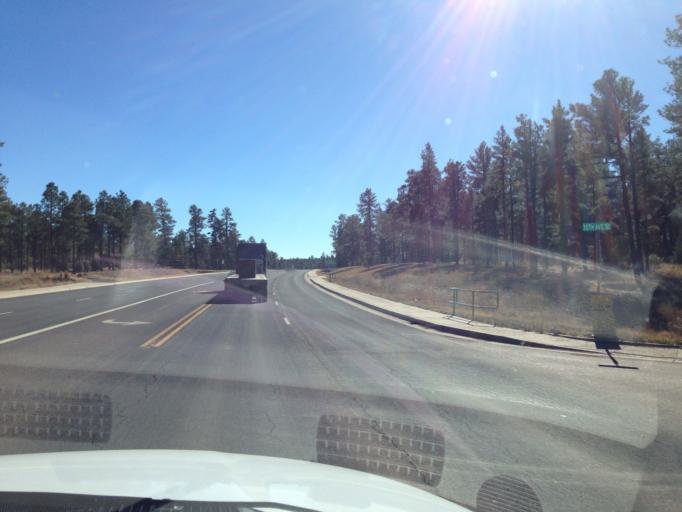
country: US
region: Arizona
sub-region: Navajo County
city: Show Low
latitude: 34.2495
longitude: -110.0741
